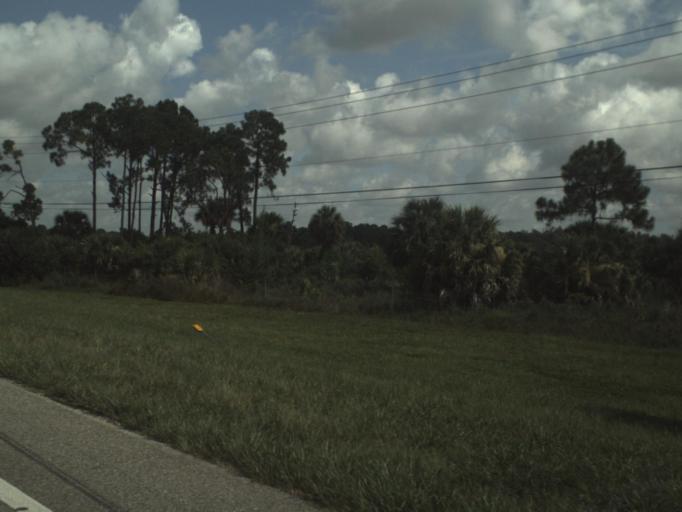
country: US
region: Florida
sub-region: Palm Beach County
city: Palm Beach Gardens
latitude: 26.7978
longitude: -80.1342
